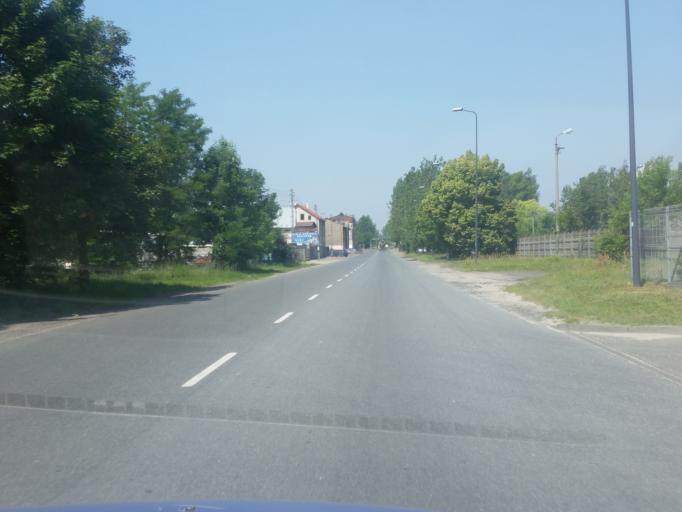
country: PL
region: Silesian Voivodeship
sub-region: Sosnowiec
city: Sosnowiec
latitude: 50.2535
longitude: 19.0988
